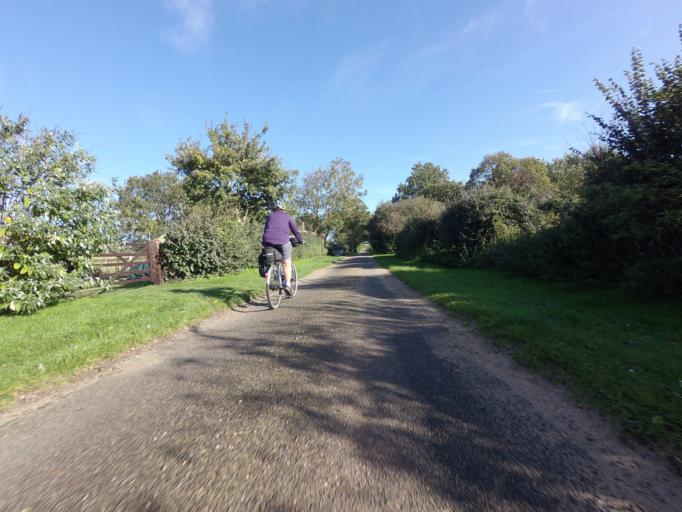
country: GB
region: England
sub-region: Norfolk
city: Fakenham
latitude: 52.8368
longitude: 0.6768
